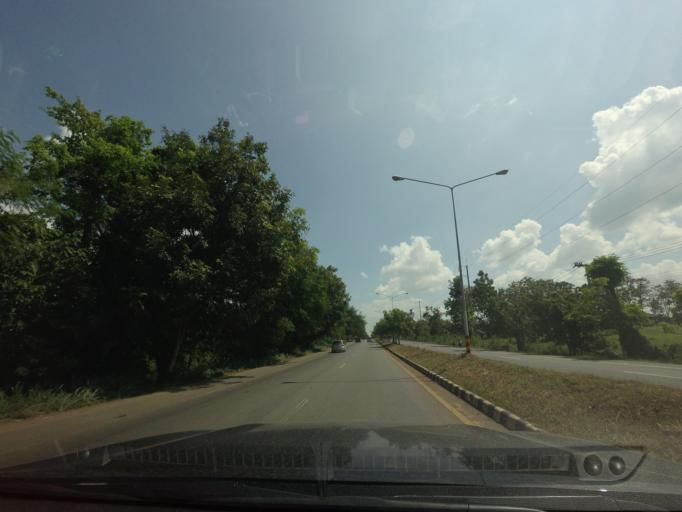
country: TH
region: Phetchabun
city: Nong Phai
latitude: 16.0619
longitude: 101.0729
